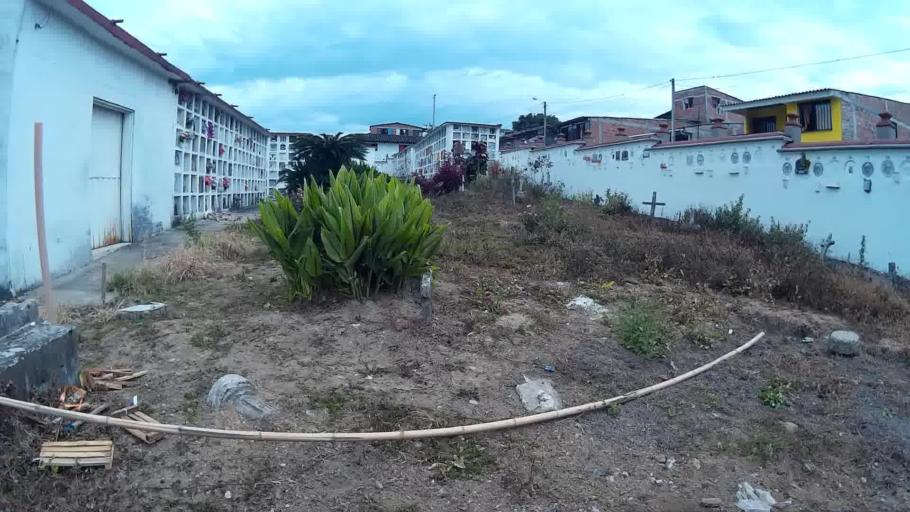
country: CO
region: Risaralda
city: Marsella
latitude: 4.9401
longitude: -75.7357
